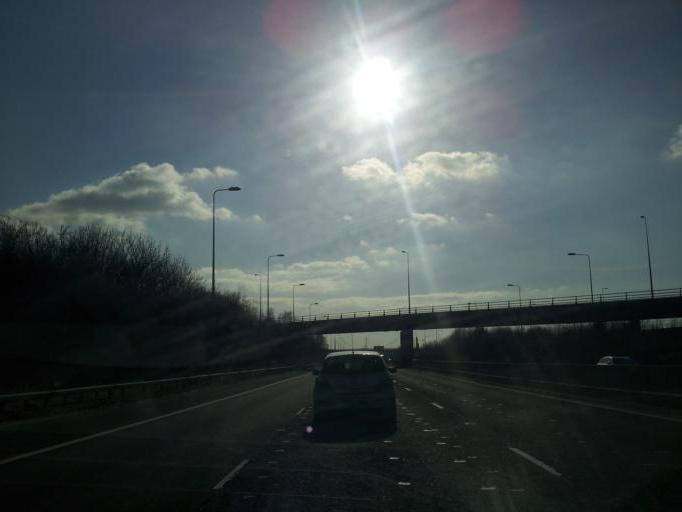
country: GB
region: England
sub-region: North Somerset
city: Easton-in-Gordano
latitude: 51.5056
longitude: -2.6665
